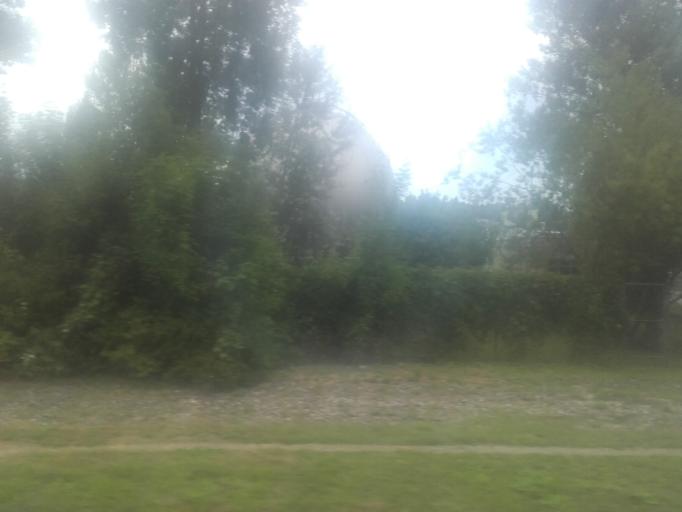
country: CH
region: Bern
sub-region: Emmental District
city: Burgdorf
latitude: 47.0647
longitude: 7.6092
